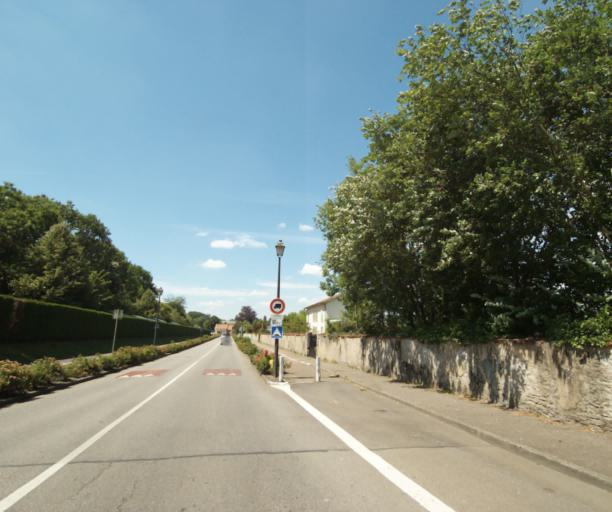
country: FR
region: Lorraine
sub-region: Departement de Meurthe-et-Moselle
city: Luneville
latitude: 48.5971
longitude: 6.5026
